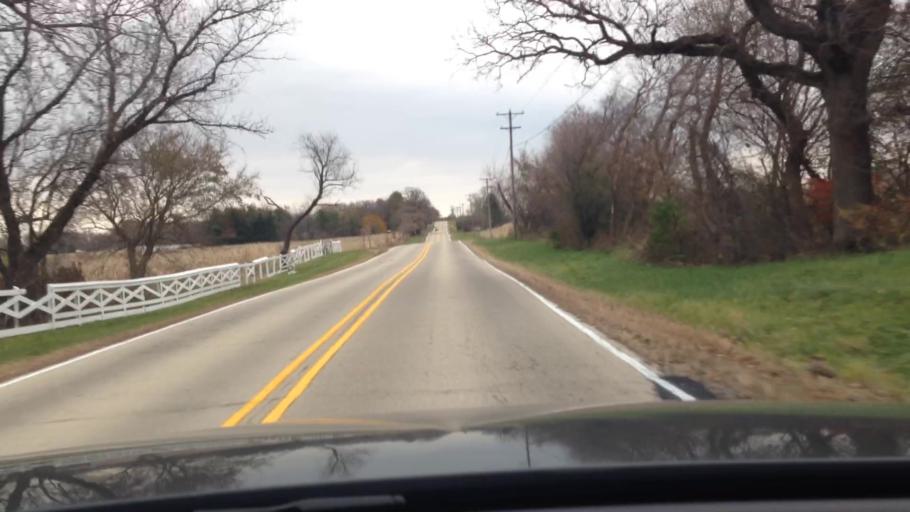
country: US
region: Illinois
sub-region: McHenry County
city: Woodstock
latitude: 42.2766
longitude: -88.4636
